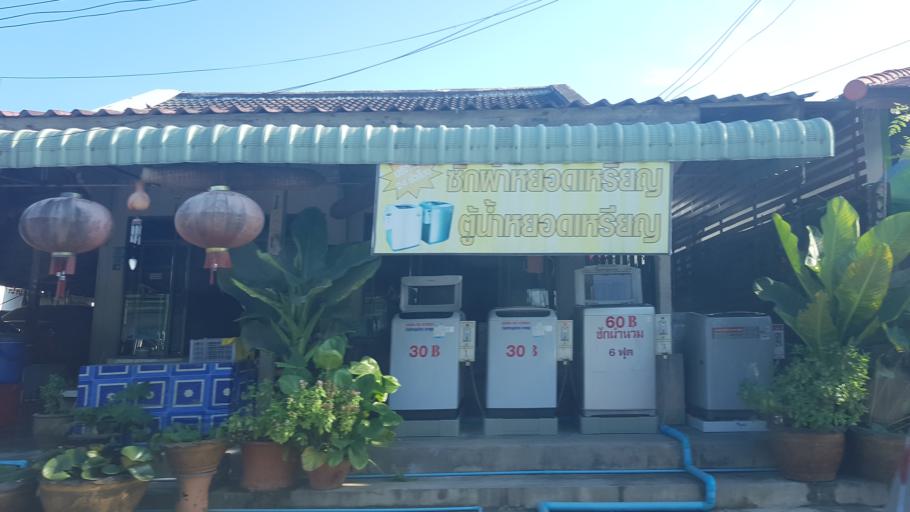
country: TH
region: Surat Thani
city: Ko Samui
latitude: 9.5582
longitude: 100.0567
